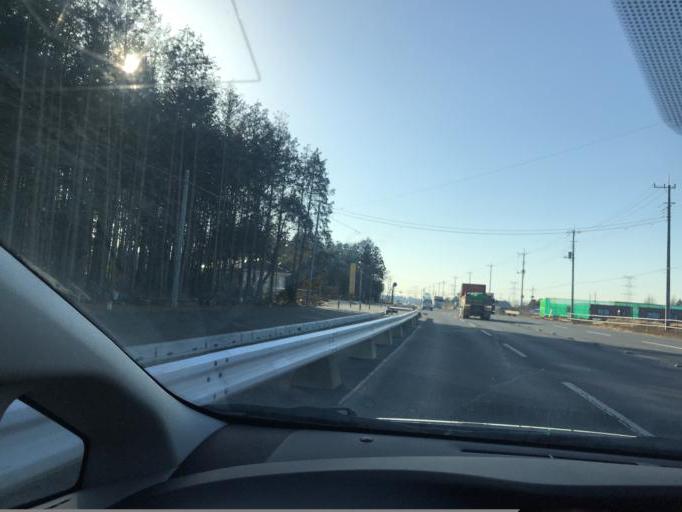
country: JP
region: Ibaraki
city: Mitsukaido
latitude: 36.0676
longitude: 140.0414
